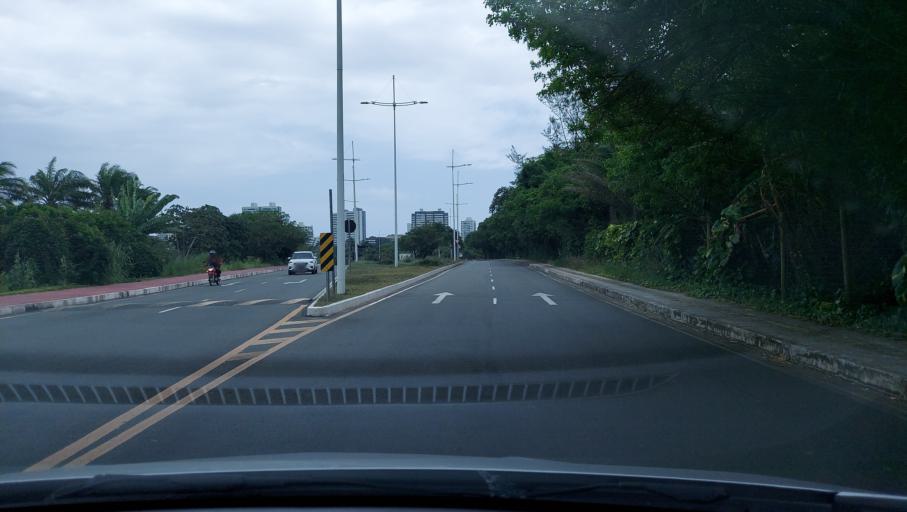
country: BR
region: Bahia
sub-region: Lauro De Freitas
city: Lauro de Freitas
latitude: -12.9546
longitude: -38.3966
